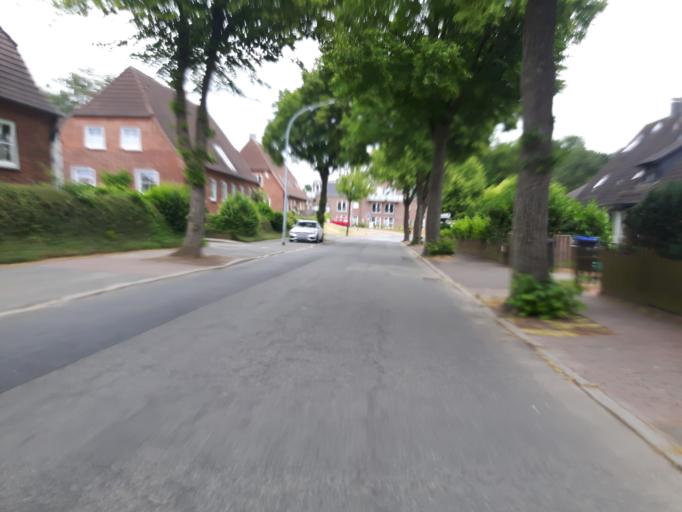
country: DE
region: Schleswig-Holstein
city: Neustadt in Holstein
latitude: 54.0909
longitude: 10.8586
